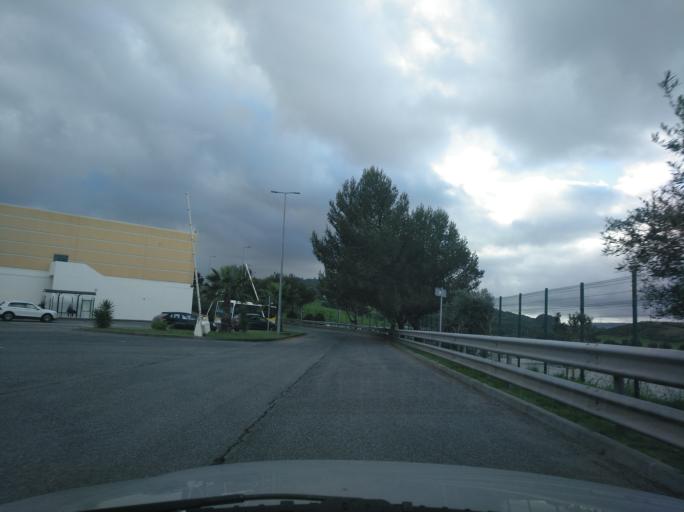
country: PT
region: Lisbon
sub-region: Loures
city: Loures
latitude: 38.8201
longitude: -9.1757
